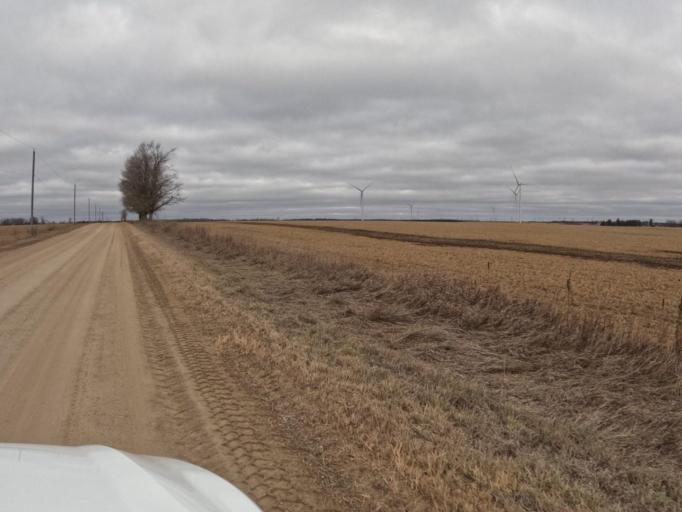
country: CA
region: Ontario
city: Shelburne
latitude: 43.8815
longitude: -80.3810
